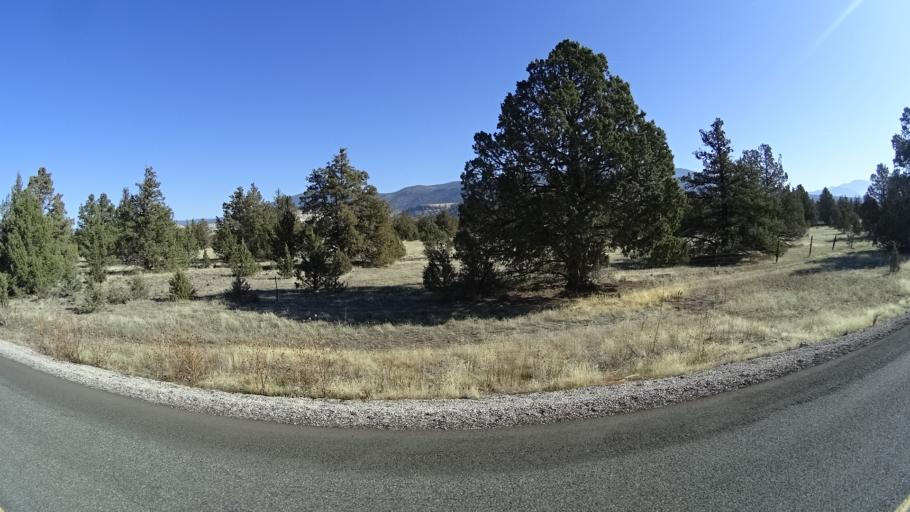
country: US
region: California
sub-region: Siskiyou County
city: Montague
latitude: 41.6478
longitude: -122.3597
